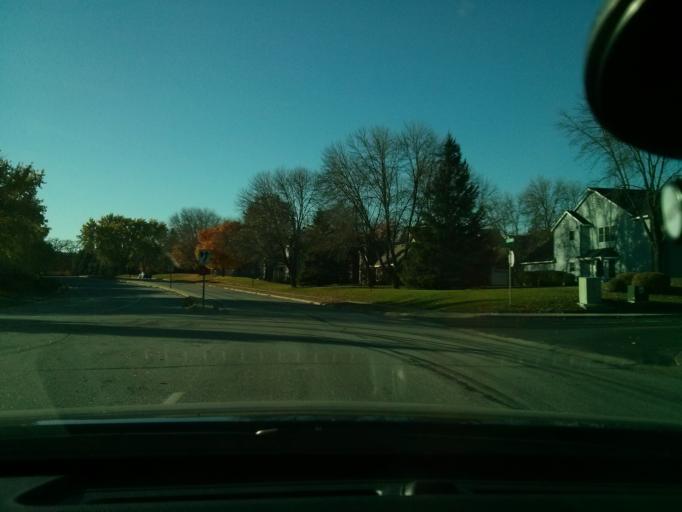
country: US
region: Minnesota
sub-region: Hennepin County
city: Eden Prairie
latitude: 44.8706
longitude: -93.4578
